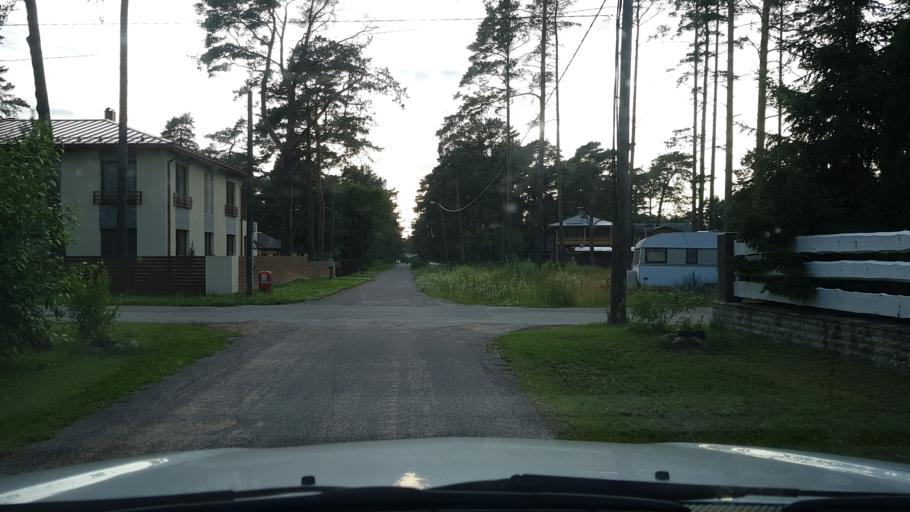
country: EE
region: Ida-Virumaa
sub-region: Narva-Joesuu linn
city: Narva-Joesuu
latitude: 59.4544
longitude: 28.0553
